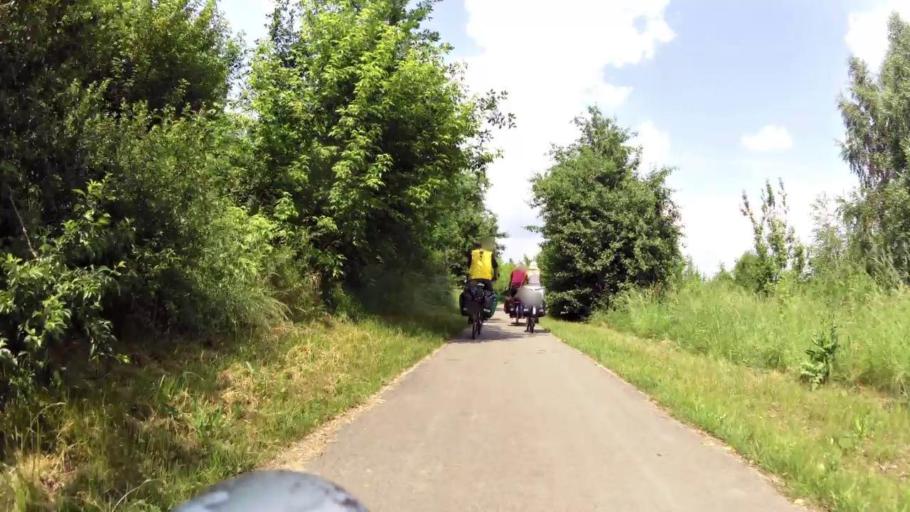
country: PL
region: Kujawsko-Pomorskie
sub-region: Powiat bydgoski
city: Koronowo
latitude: 53.2903
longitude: 17.9466
